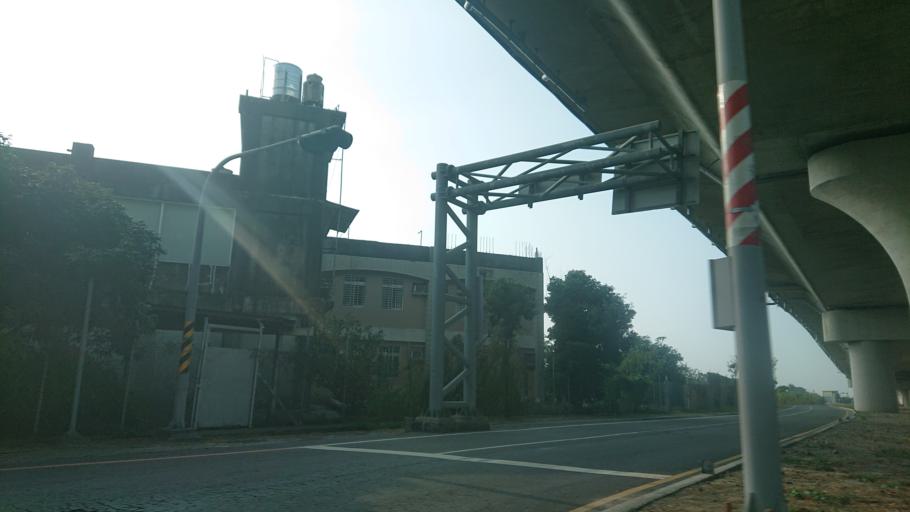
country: TW
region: Taiwan
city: Xinying
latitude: 23.1939
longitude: 120.2712
